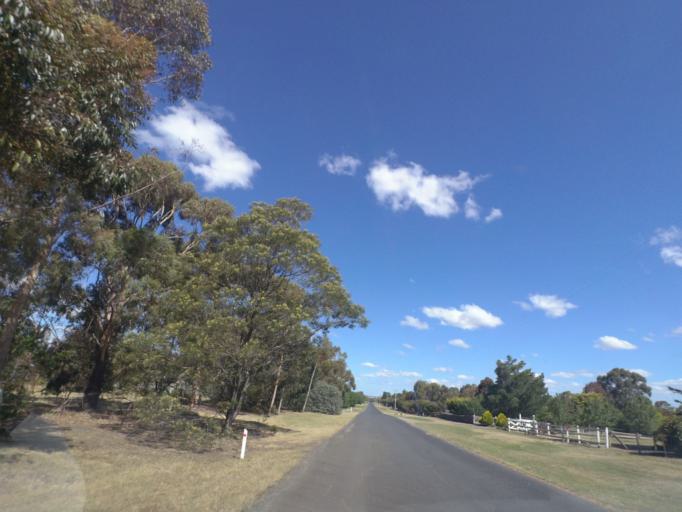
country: AU
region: Victoria
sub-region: Hume
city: Sunbury
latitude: -37.4569
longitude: 144.6642
